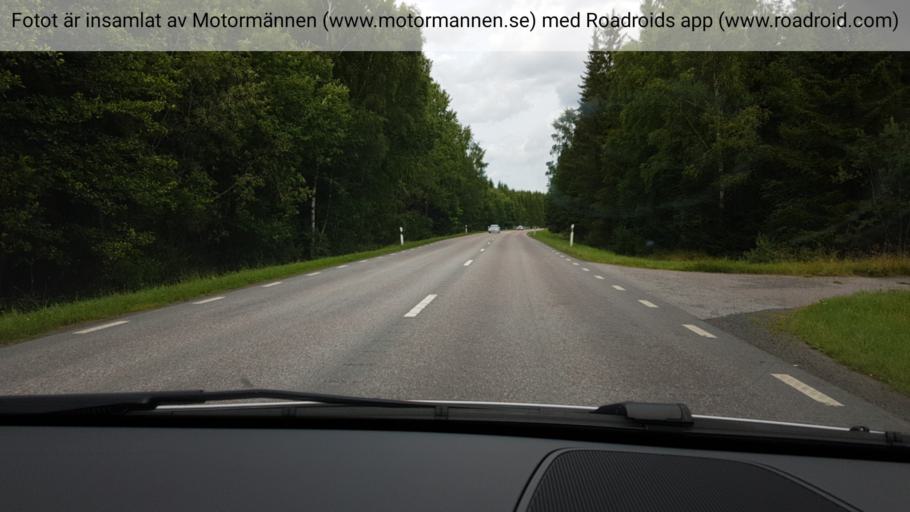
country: SE
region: Uppsala
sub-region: Osthammars Kommun
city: Gimo
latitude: 60.1892
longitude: 18.1901
